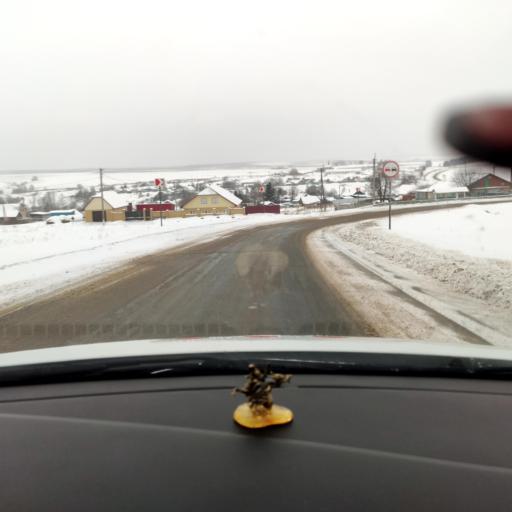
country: RU
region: Tatarstan
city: Vysokaya Gora
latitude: 56.0995
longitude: 49.1263
